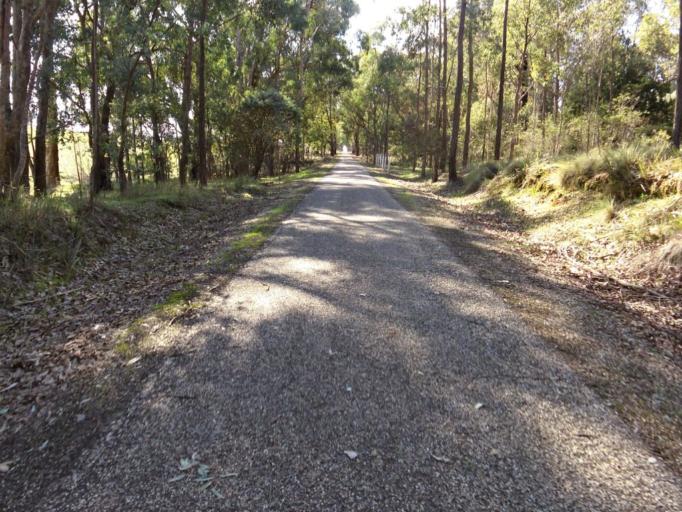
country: AU
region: Victoria
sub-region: Wangaratta
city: Wangaratta
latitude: -36.4021
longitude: 146.6426
